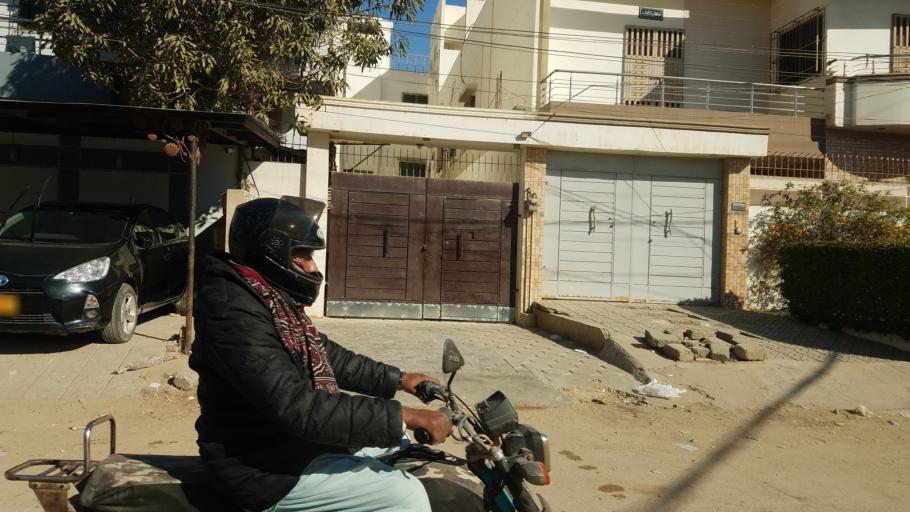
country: PK
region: Sindh
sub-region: Karachi District
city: Karachi
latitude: 24.9273
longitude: 67.0528
